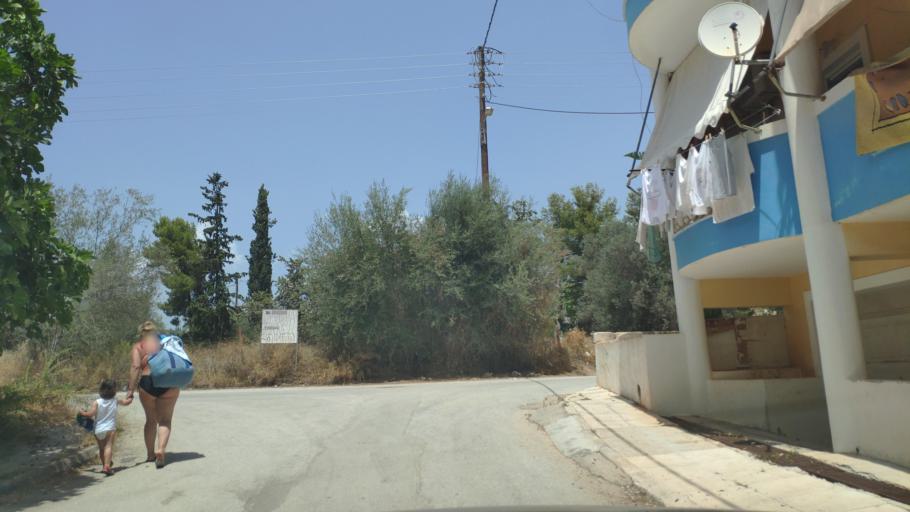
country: GR
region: Peloponnese
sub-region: Nomos Argolidos
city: Porto Cheli
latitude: 37.3292
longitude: 23.1485
